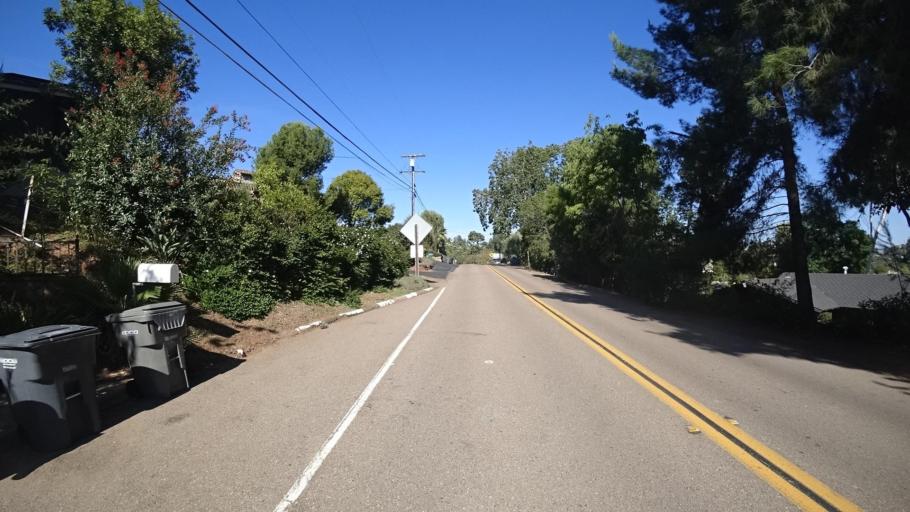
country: US
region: California
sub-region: San Diego County
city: Casa de Oro-Mount Helix
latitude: 32.7605
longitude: -116.9776
